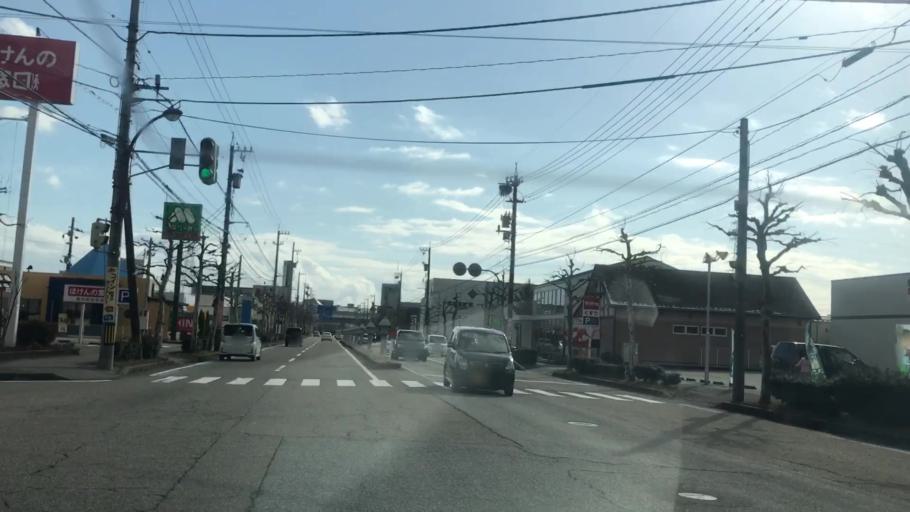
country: JP
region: Toyama
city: Takaoka
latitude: 36.7308
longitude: 137.0154
